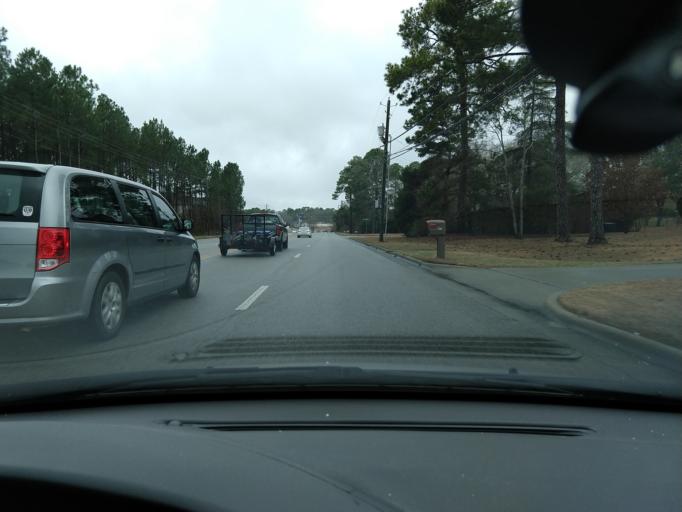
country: US
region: Alabama
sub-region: Houston County
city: Dothan
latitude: 31.2589
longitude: -85.4287
